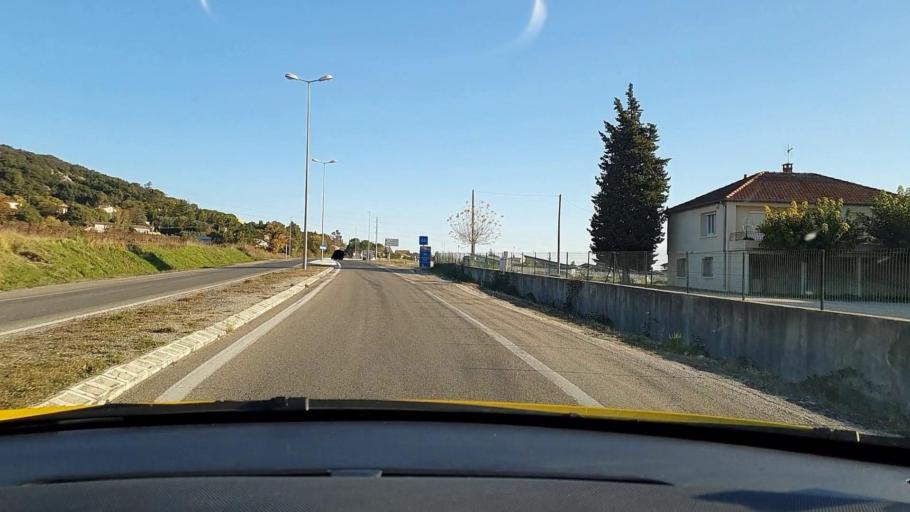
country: FR
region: Languedoc-Roussillon
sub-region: Departement du Gard
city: Saint-Julien-les-Rosiers
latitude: 44.1554
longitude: 4.1106
